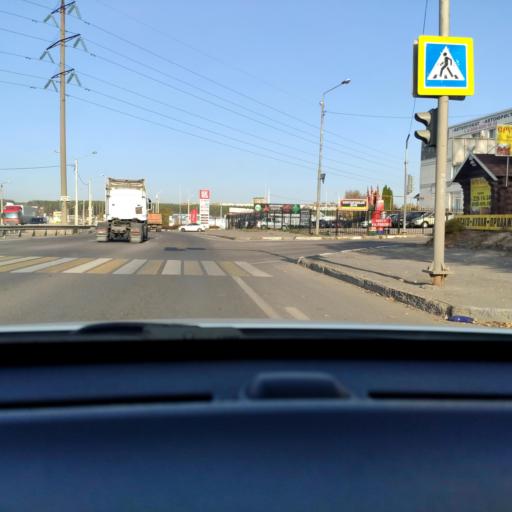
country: RU
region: Voronezj
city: Voronezh
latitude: 51.6664
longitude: 39.1273
